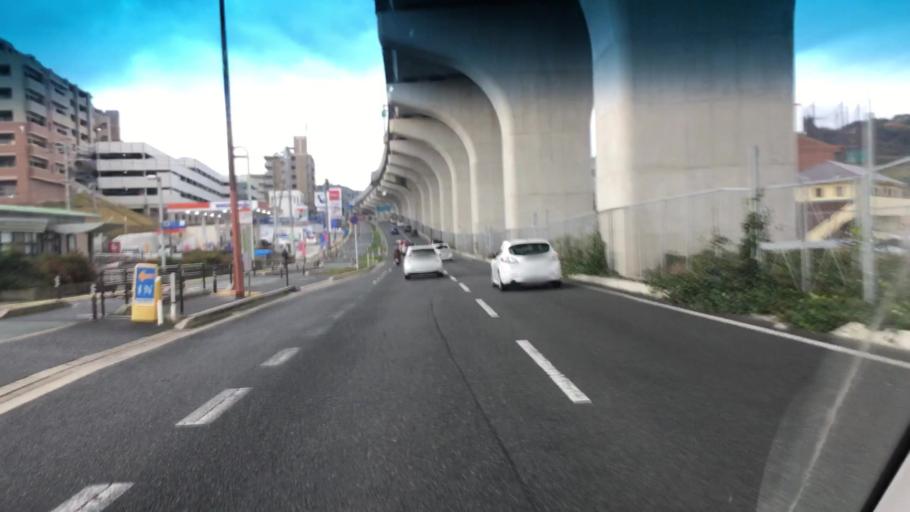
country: JP
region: Fukuoka
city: Maebaru-chuo
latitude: 33.5691
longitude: 130.3018
